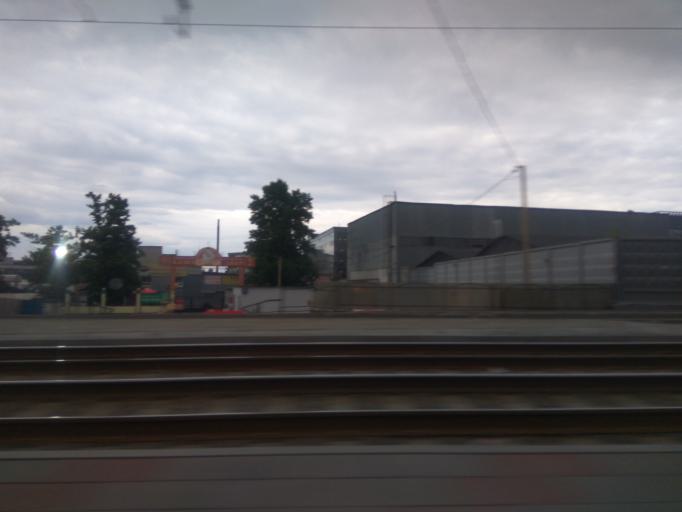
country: RU
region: Moscow
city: Nagornyy
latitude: 55.6731
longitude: 37.6276
